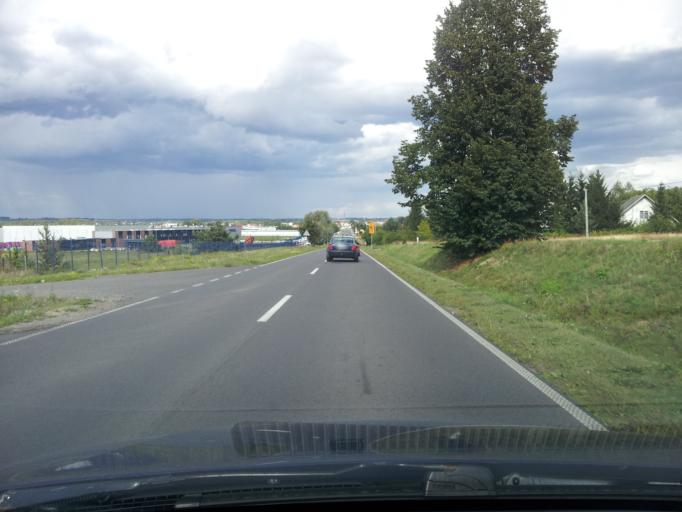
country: PL
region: Kujawsko-Pomorskie
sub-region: Powiat brodnicki
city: Brodnica
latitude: 53.2257
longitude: 19.3868
